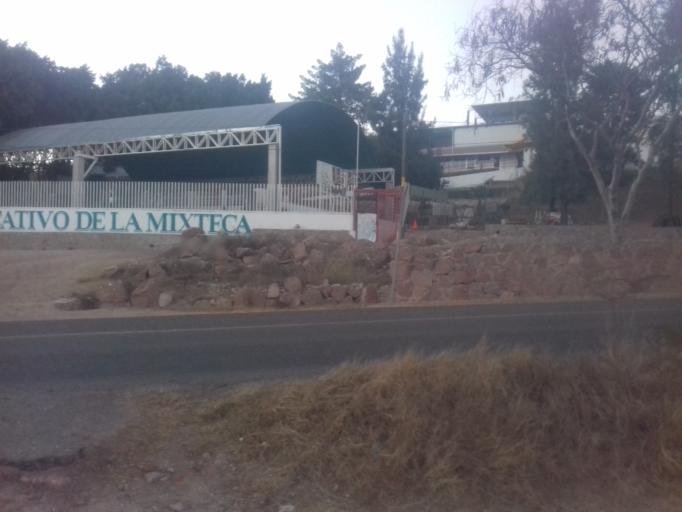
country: MX
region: Oaxaca
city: Ciudad de Huajuapam de Leon
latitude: 17.8239
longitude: -97.7917
